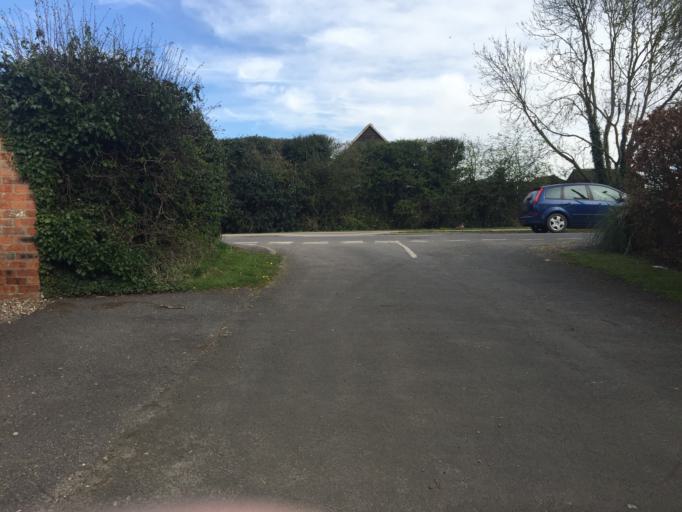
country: GB
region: England
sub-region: Lincolnshire
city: Skellingthorpe
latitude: 53.1254
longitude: -0.6420
